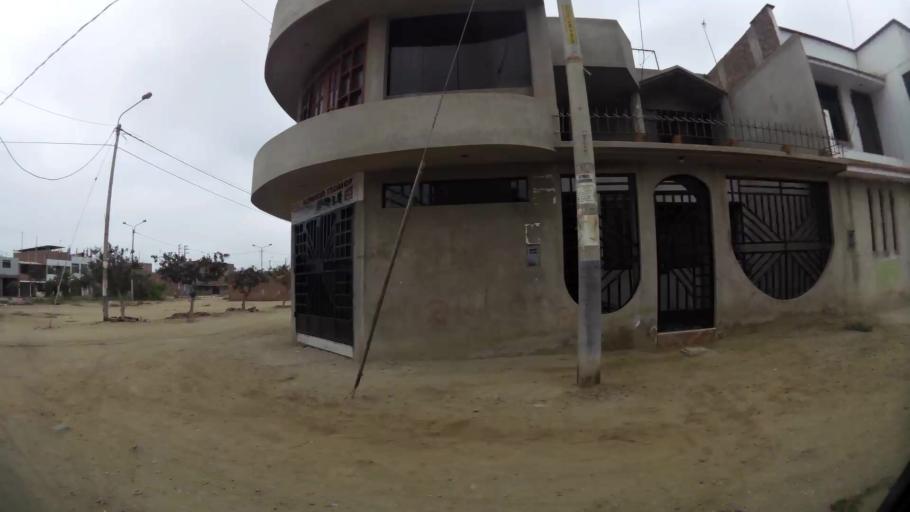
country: PE
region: La Libertad
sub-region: Provincia de Trujillo
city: La Esperanza
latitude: -8.0881
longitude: -79.0451
